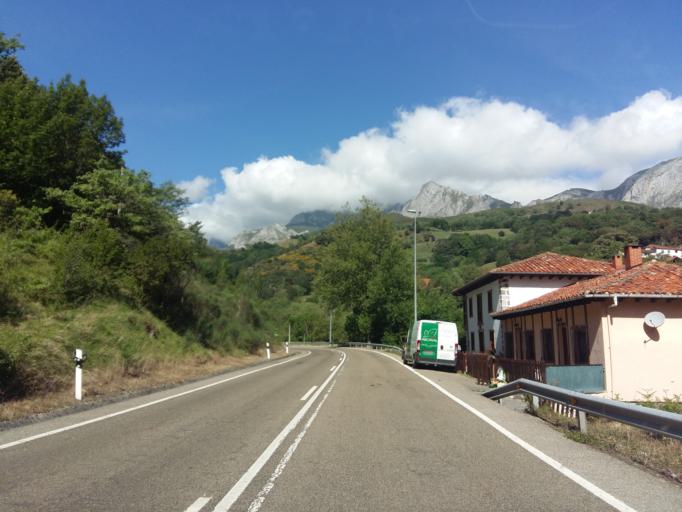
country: ES
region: Cantabria
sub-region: Provincia de Cantabria
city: Potes
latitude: 43.1962
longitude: -4.5990
